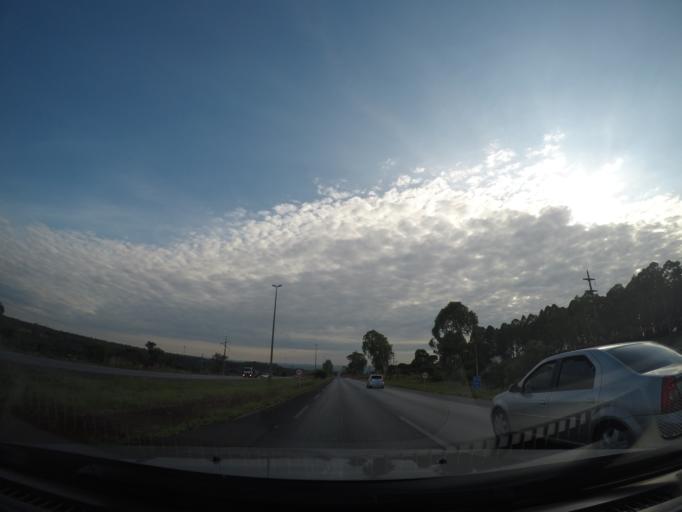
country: BR
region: Goias
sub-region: Planaltina
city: Planaltina
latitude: -15.6263
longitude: -47.7258
